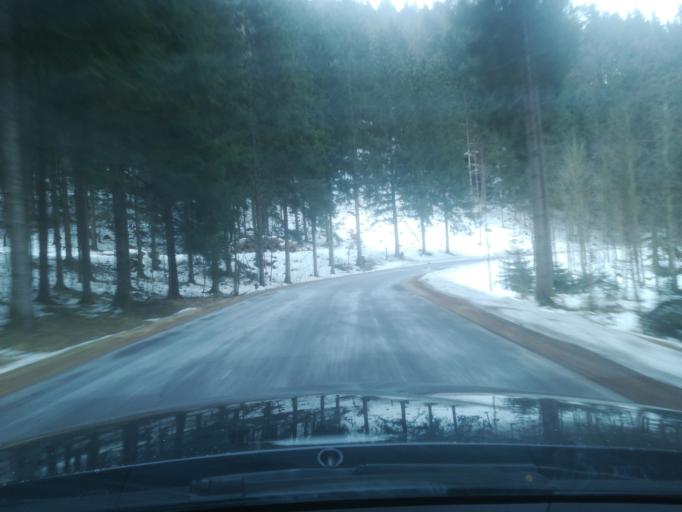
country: AT
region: Upper Austria
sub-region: Politischer Bezirk Perg
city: Perg
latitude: 48.4057
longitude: 14.6363
